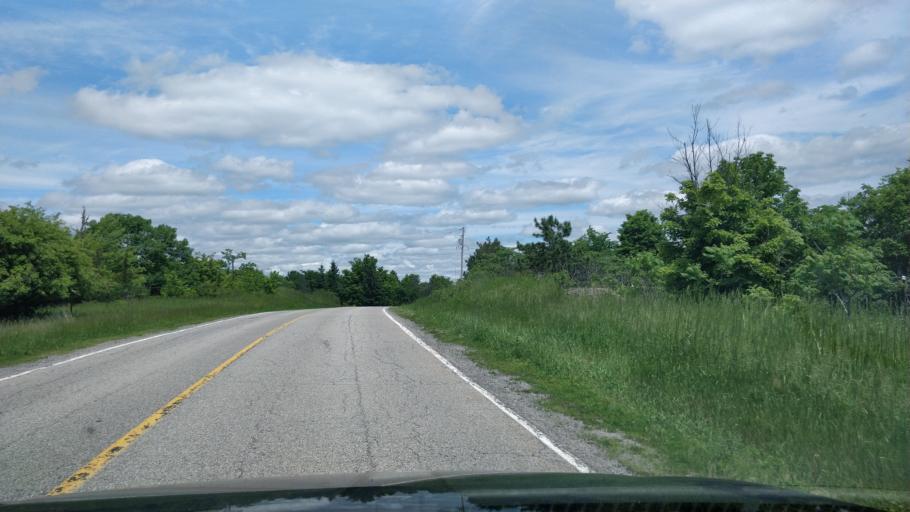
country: CA
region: Ontario
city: Perth
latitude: 44.7459
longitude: -76.4939
